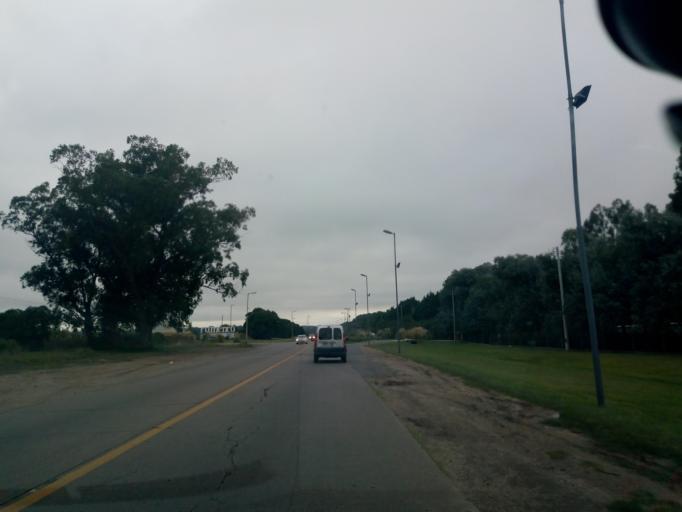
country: AR
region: Buenos Aires
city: Mar del Plata
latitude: -38.0782
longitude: -57.5824
